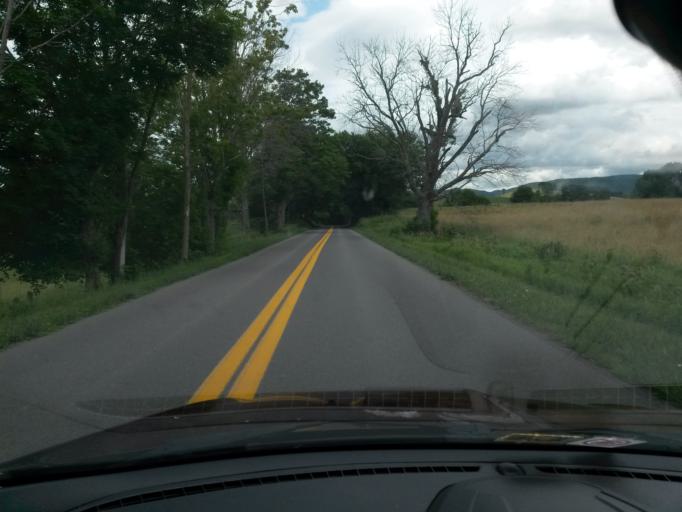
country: US
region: West Virginia
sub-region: Monroe County
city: Union
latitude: 37.5497
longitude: -80.5289
